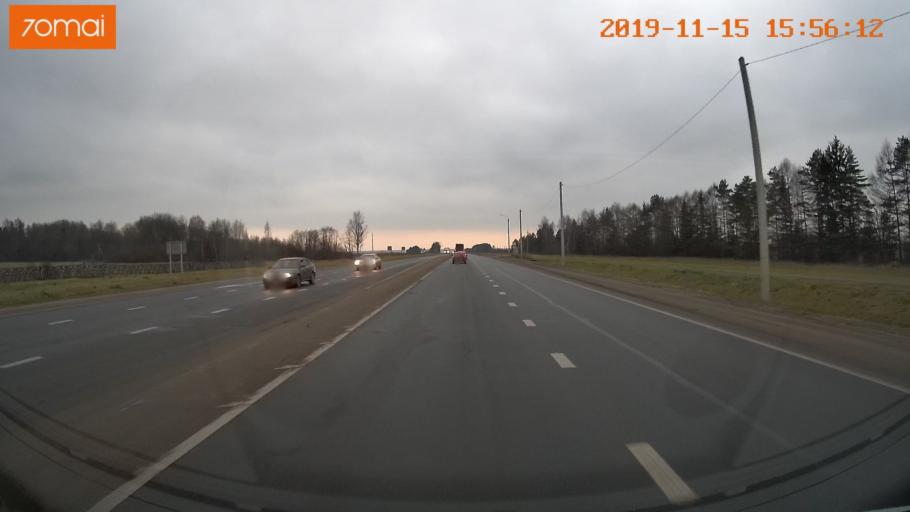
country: RU
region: Jaroslavl
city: Yaroslavl
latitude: 57.8448
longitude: 39.9760
